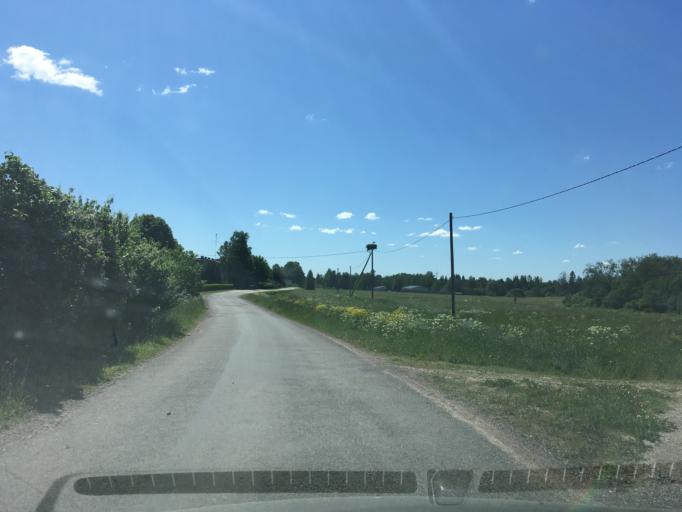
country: EE
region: Harju
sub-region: Rae vald
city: Vaida
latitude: 59.1677
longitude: 25.1244
